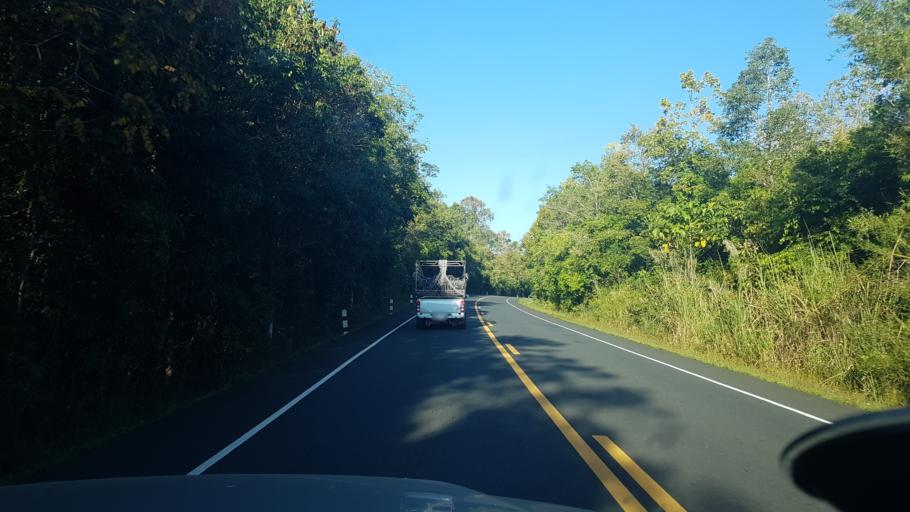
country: TH
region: Phetchabun
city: Nam Nao
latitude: 16.7027
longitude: 101.6099
